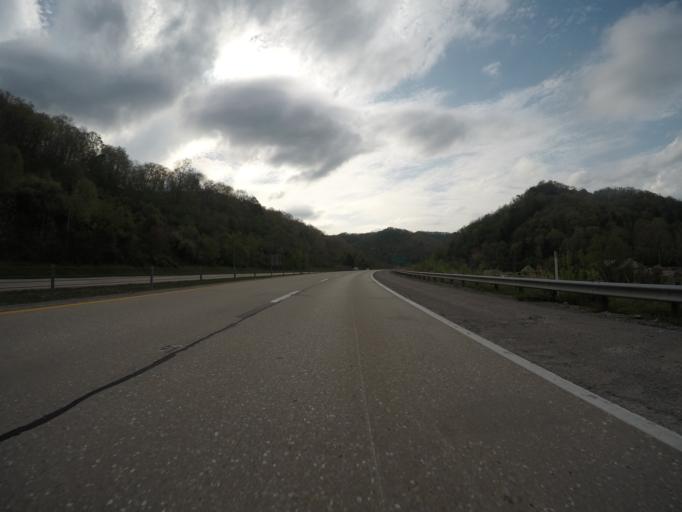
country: US
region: West Virginia
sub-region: Boone County
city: Madison
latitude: 38.1043
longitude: -81.8435
